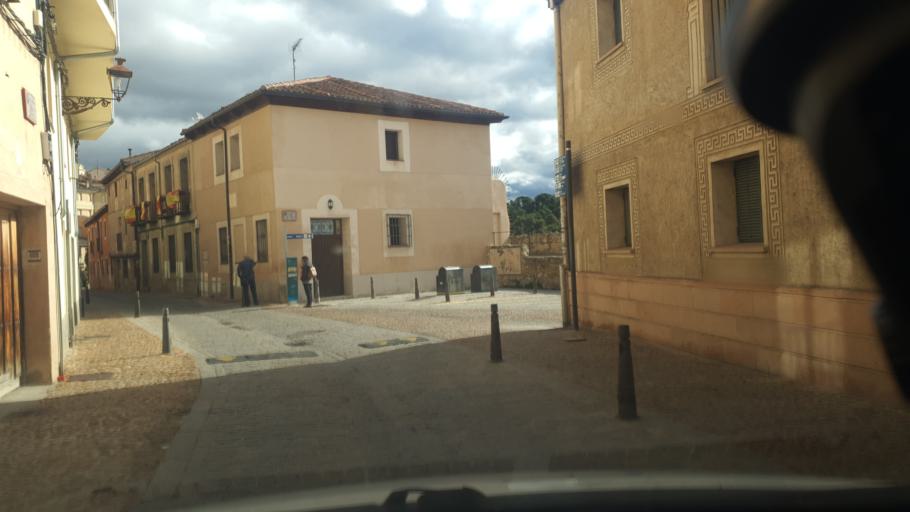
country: ES
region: Castille and Leon
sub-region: Provincia de Segovia
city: Segovia
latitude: 40.9506
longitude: -4.1285
